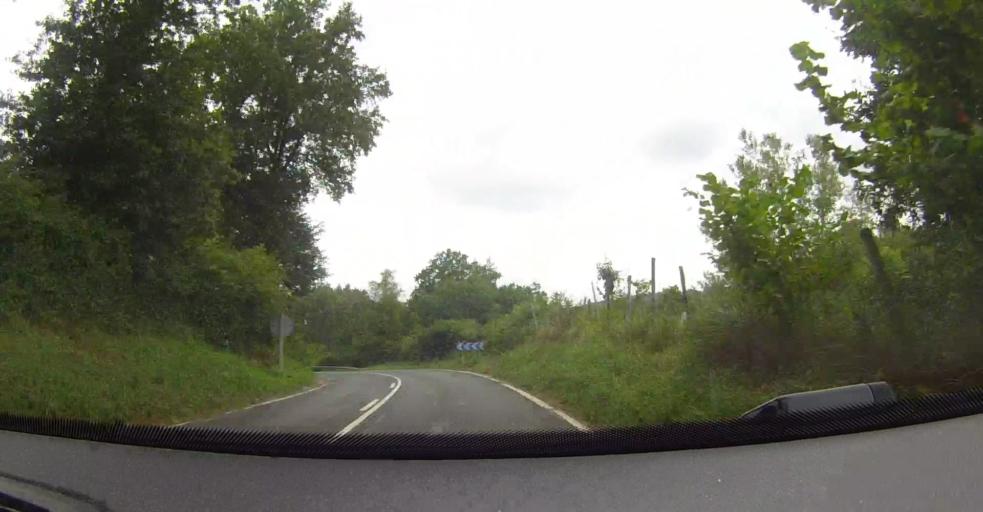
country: ES
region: Basque Country
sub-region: Bizkaia
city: Balmaseda
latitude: 43.2407
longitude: -3.2206
